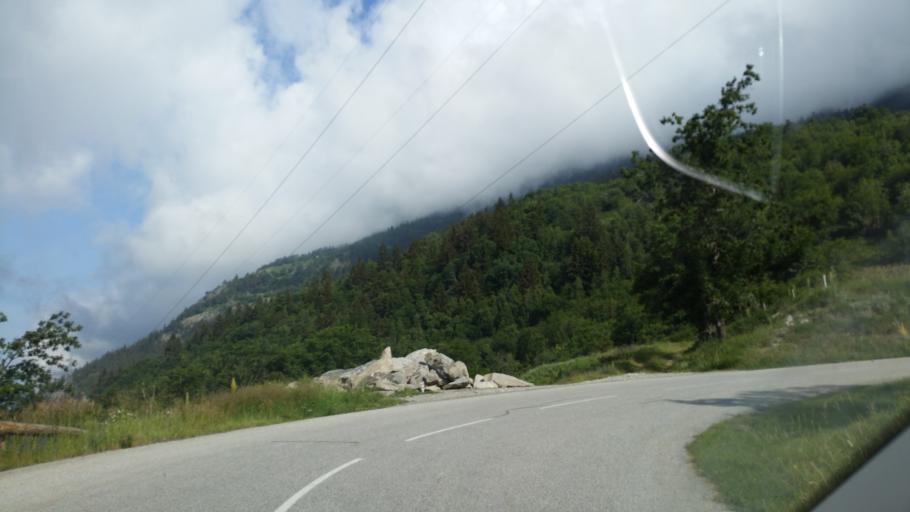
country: FR
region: Rhone-Alpes
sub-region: Departement de la Savoie
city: Modane
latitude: 45.2098
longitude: 6.5961
